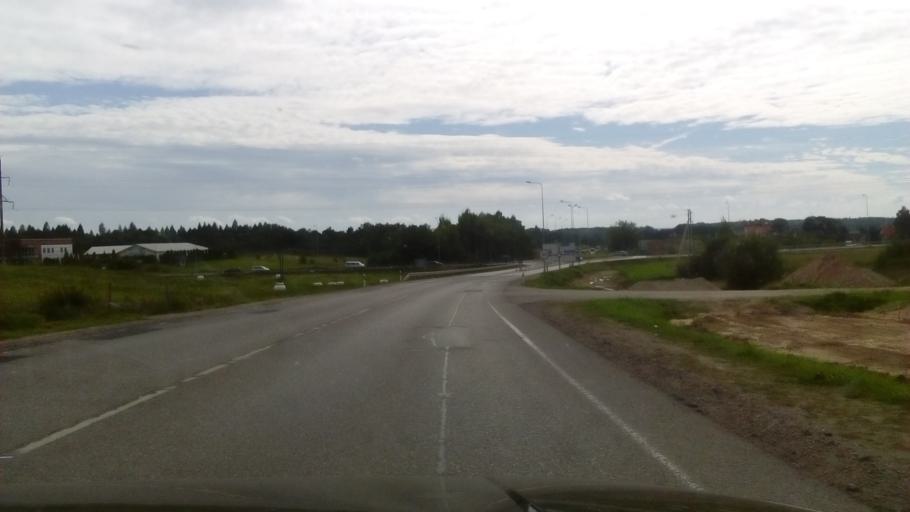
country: LT
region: Alytaus apskritis
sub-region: Alytus
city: Alytus
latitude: 54.3901
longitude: 23.9982
